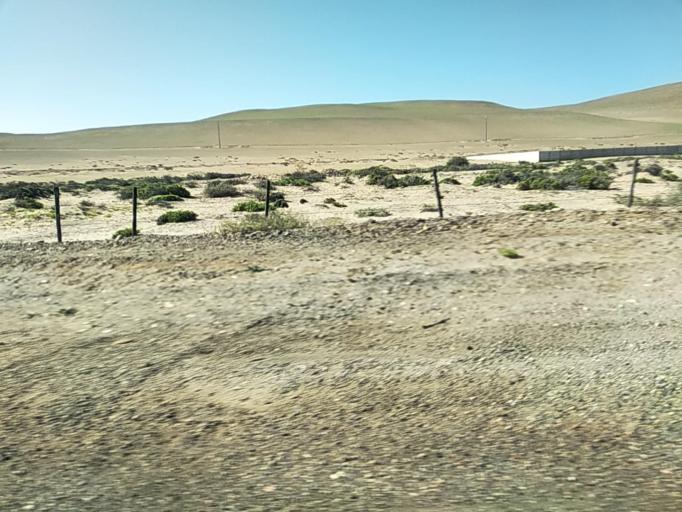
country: CL
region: Atacama
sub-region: Provincia de Copiapo
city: Copiapo
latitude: -27.3461
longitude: -70.7417
